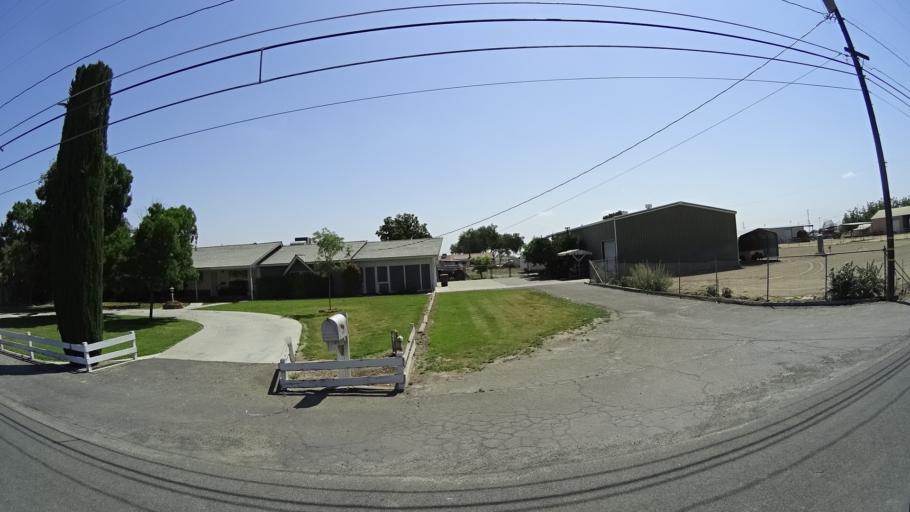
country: US
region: California
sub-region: Kings County
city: Home Garden
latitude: 36.3159
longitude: -119.6213
